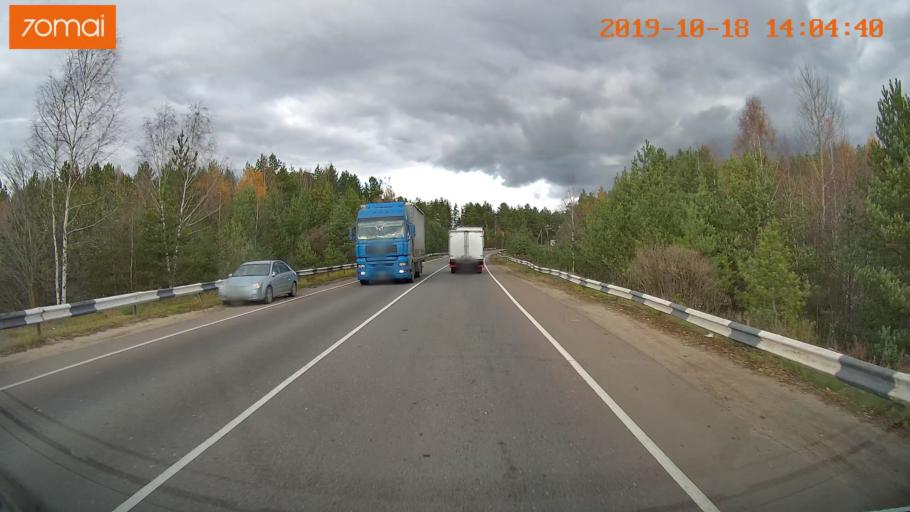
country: RU
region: Rjazan
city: Spas-Klepiki
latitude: 55.1282
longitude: 40.1336
